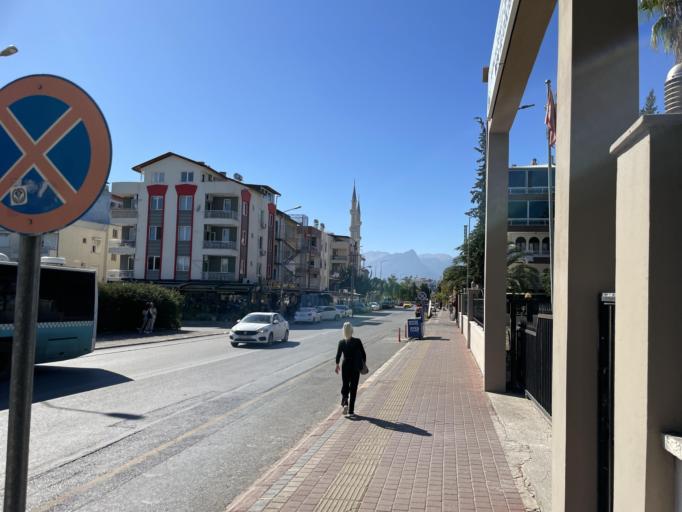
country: TR
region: Antalya
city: Antalya
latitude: 36.9047
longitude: 30.6632
